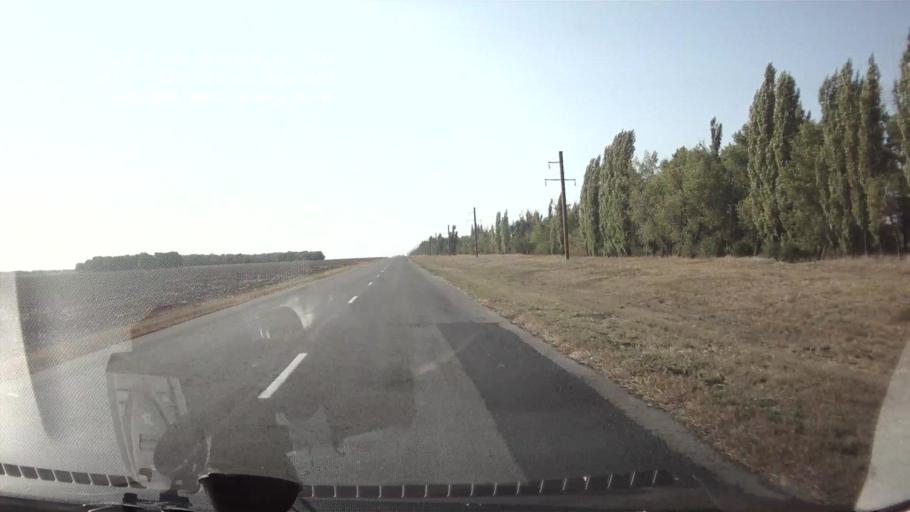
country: RU
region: Rostov
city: Tselina
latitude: 46.5324
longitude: 40.8998
